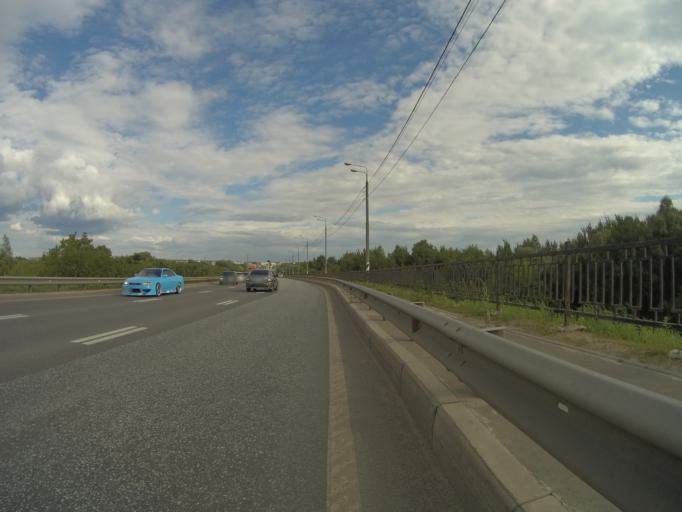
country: RU
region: Vladimir
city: Vladimir
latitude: 56.1201
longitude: 40.4124
